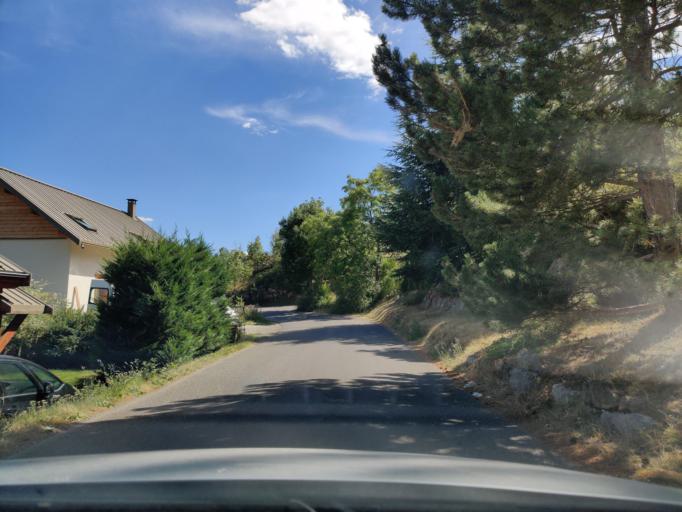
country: FR
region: Provence-Alpes-Cote d'Azur
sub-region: Departement des Hautes-Alpes
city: Saint-Martin-de-Queyrieres
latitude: 44.7394
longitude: 6.5677
